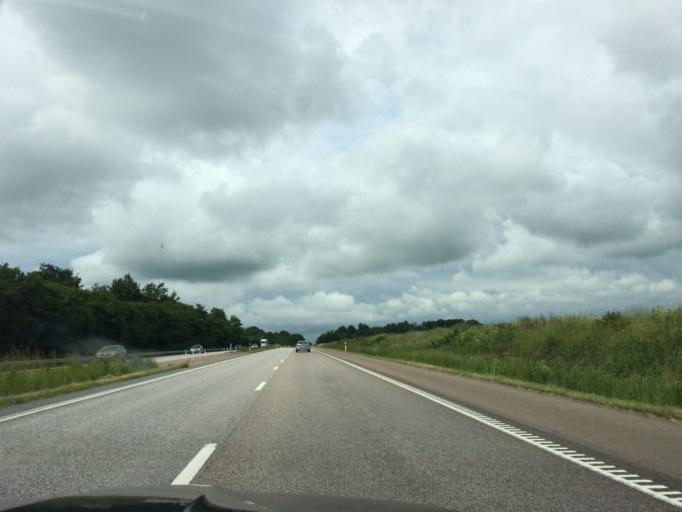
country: SE
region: Skane
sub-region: Angelholms Kommun
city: Strovelstorp
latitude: 56.1527
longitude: 12.8443
